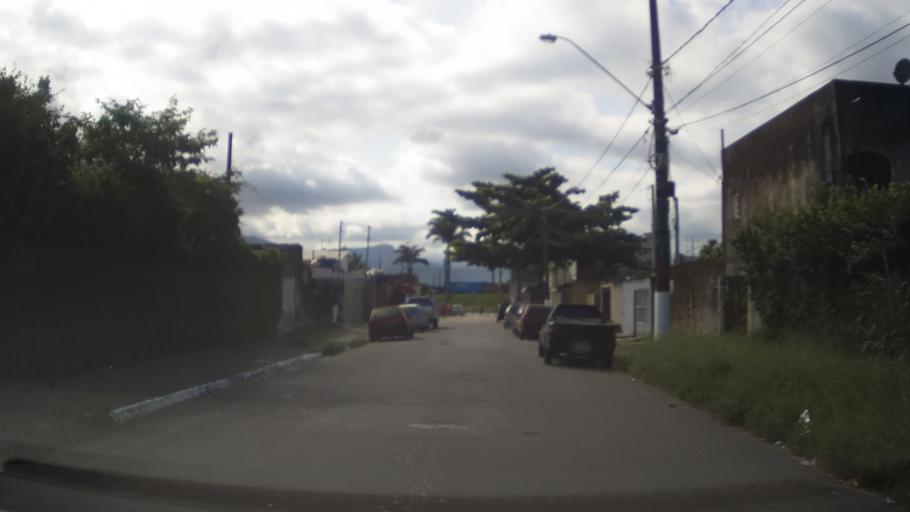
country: BR
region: Sao Paulo
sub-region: Praia Grande
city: Praia Grande
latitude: -24.0150
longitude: -46.4540
